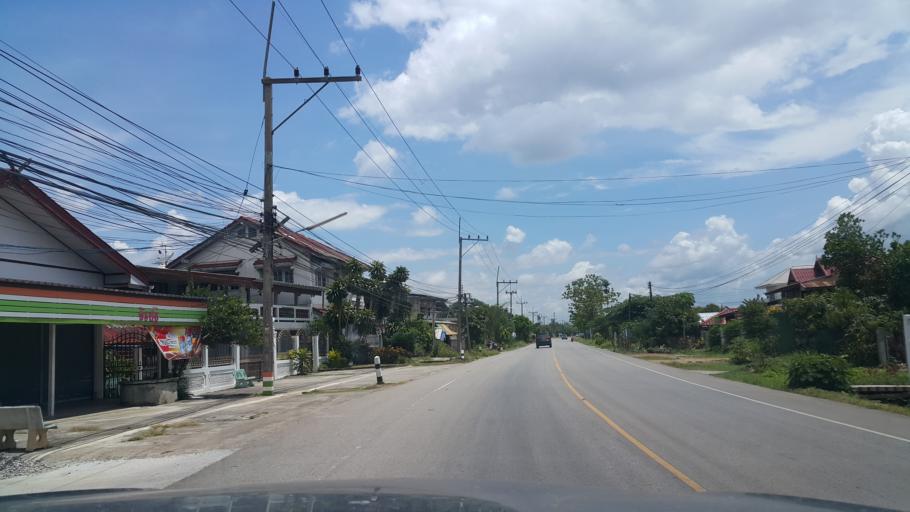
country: TH
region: Phayao
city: Phayao
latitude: 19.1812
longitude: 99.8362
